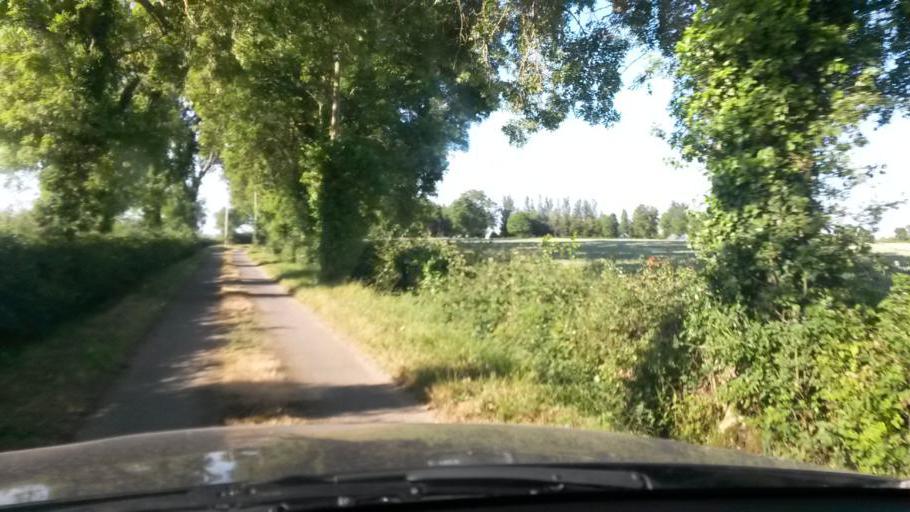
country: IE
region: Leinster
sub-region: Dublin City
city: Finglas
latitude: 53.4428
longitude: -6.3179
